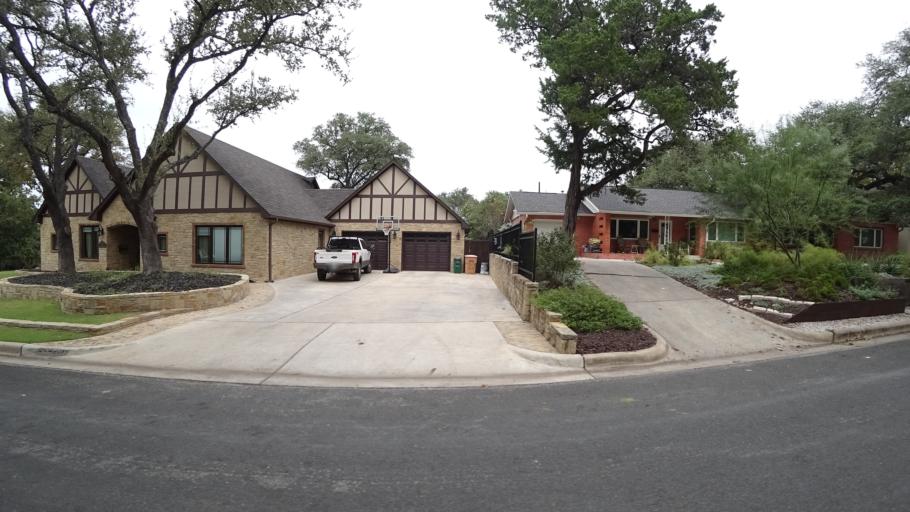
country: US
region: Texas
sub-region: Travis County
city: Austin
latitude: 30.2954
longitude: -97.7254
